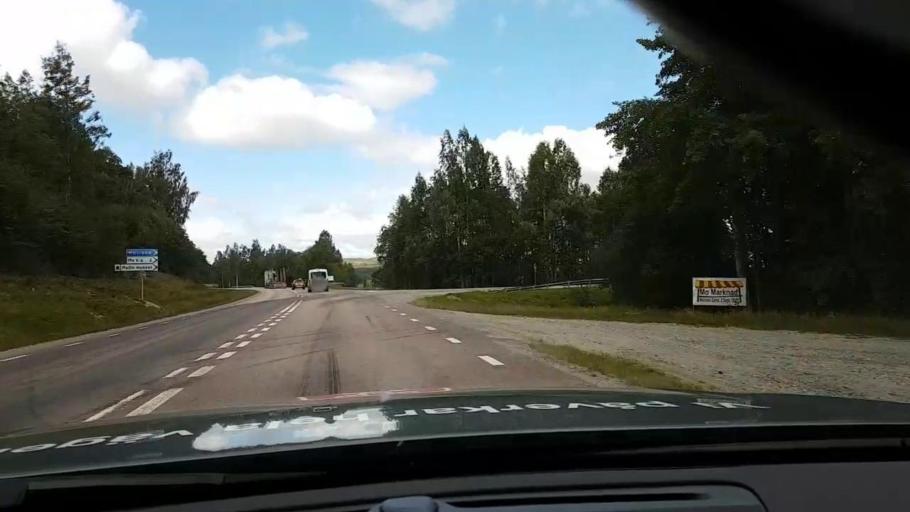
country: SE
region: Vaesternorrland
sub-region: OErnskoeldsviks Kommun
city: Bjasta
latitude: 63.3616
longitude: 18.4625
